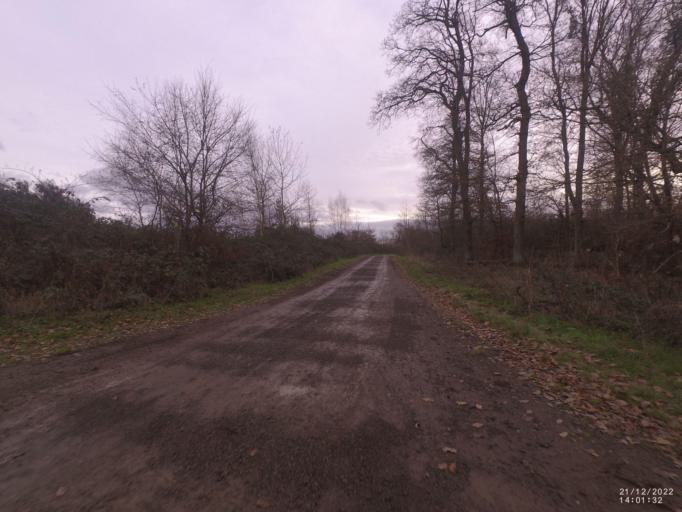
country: DE
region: Rheinland-Pfalz
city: Waldorf
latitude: 50.5084
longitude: 7.2443
